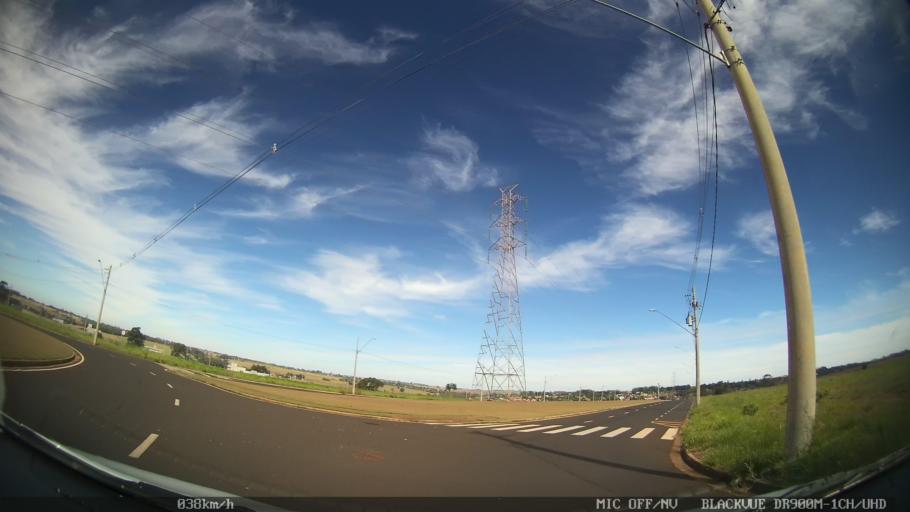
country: BR
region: Sao Paulo
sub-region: Sao Jose Do Rio Preto
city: Sao Jose do Rio Preto
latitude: -20.8512
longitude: -49.3755
